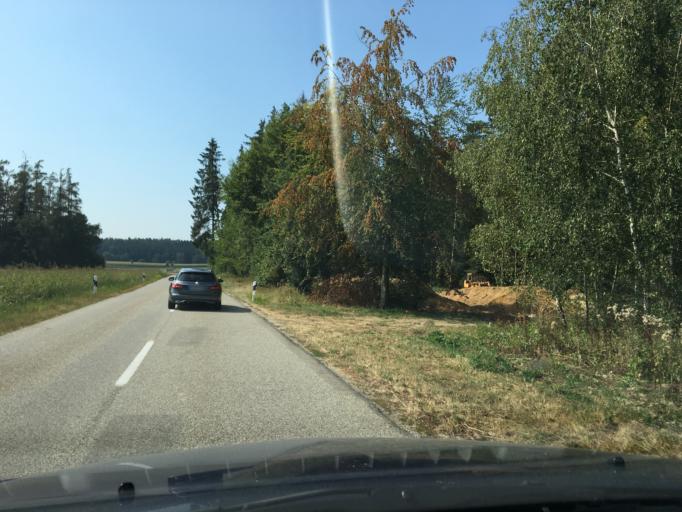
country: DE
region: Bavaria
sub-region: Upper Bavaria
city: Niederbergkirchen
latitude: 48.3302
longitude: 12.4824
